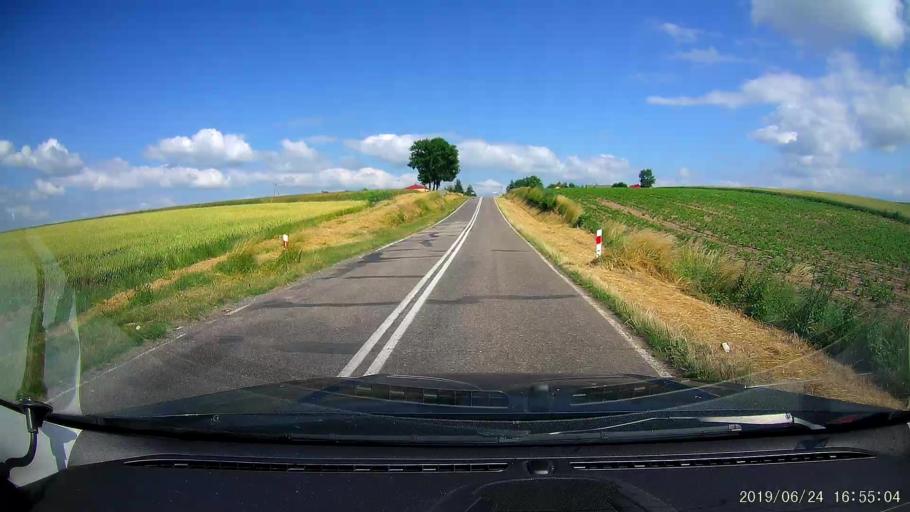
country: PL
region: Lublin Voivodeship
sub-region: Powiat tomaszowski
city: Telatyn
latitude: 50.5297
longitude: 23.8255
